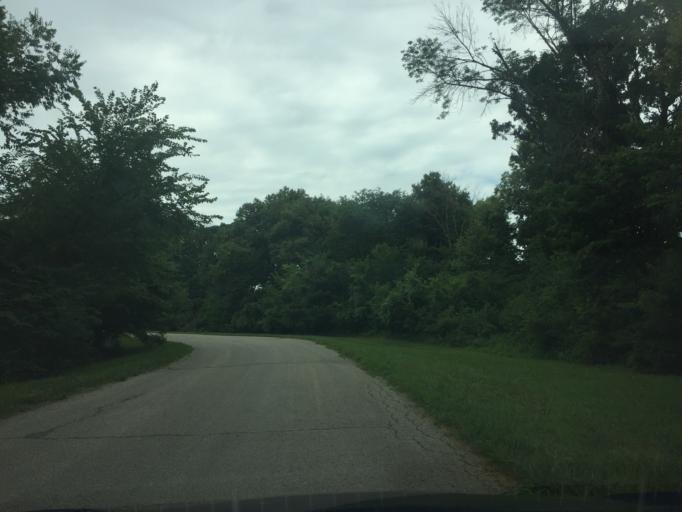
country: US
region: Missouri
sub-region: Platte County
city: Weston
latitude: 39.3722
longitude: -94.9275
